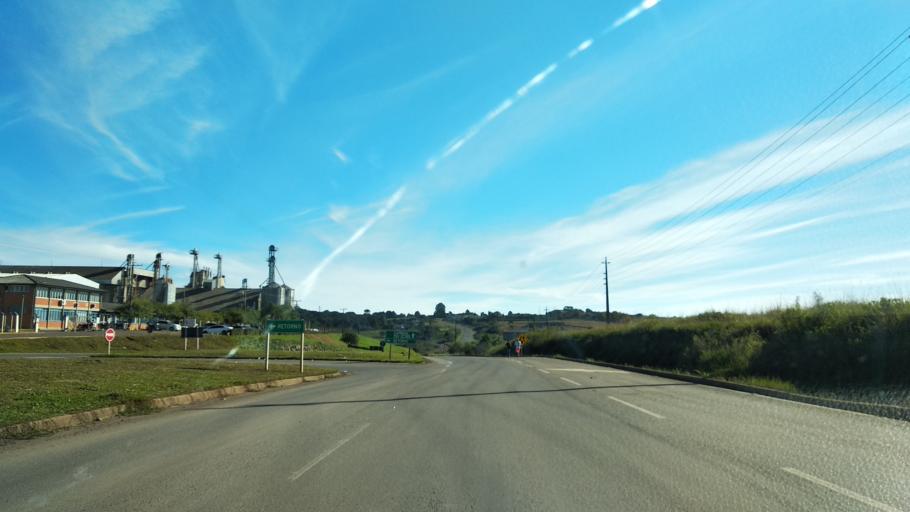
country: BR
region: Santa Catarina
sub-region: Campos Novos
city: Campos Novos
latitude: -27.4083
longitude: -51.2150
